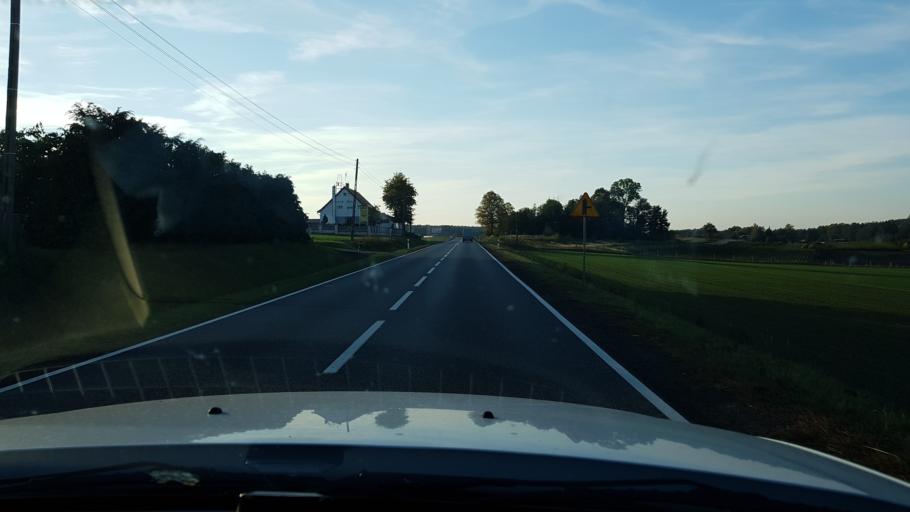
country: PL
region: West Pomeranian Voivodeship
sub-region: Powiat gryfinski
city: Chojna
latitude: 52.9643
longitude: 14.4062
